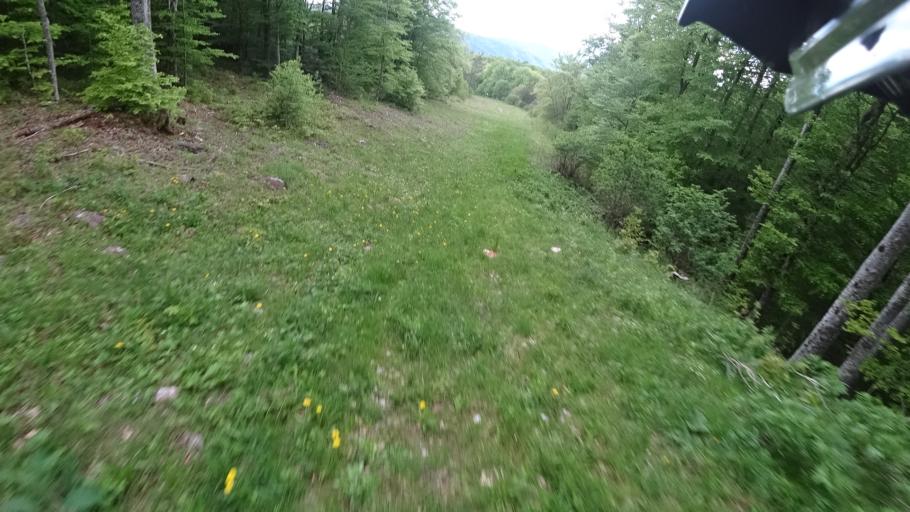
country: HR
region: Karlovacka
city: Plaski
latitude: 44.9077
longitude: 15.4187
